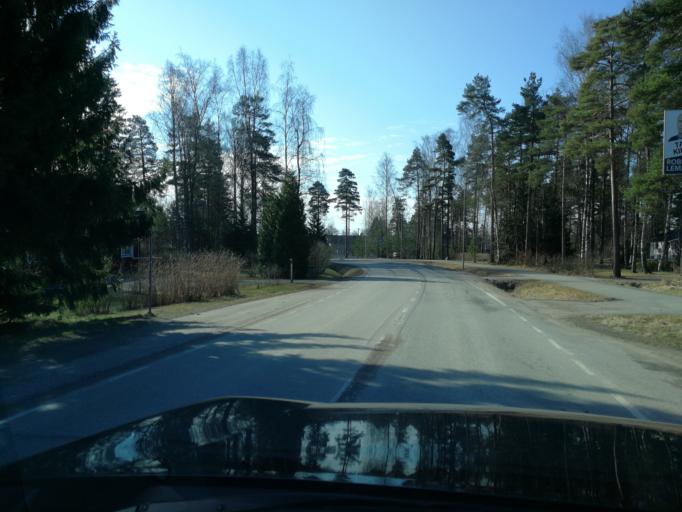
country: FI
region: Uusimaa
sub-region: Raaseporin
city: Inga
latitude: 60.0500
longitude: 24.0145
